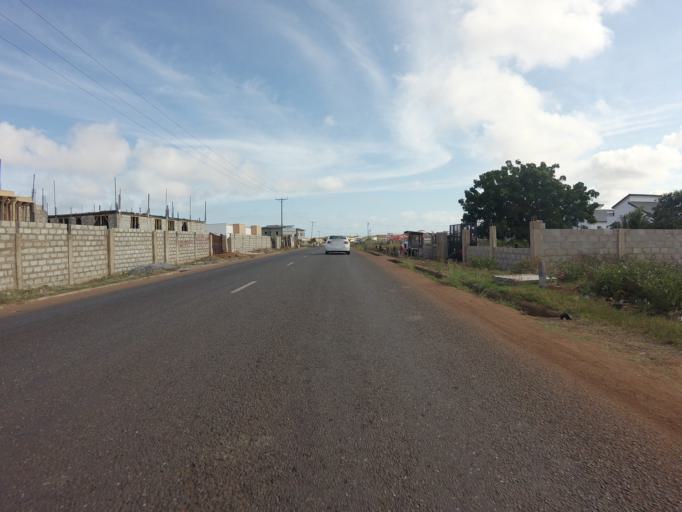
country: GH
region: Greater Accra
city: Teshi Old Town
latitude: 5.5924
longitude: -0.1362
